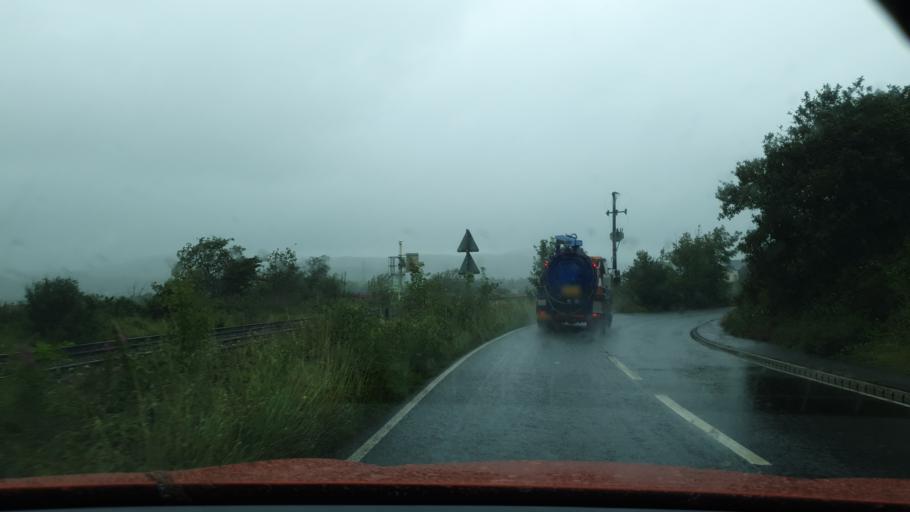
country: GB
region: England
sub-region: Cumbria
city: Askam in Furness
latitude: 54.2569
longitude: -3.2139
